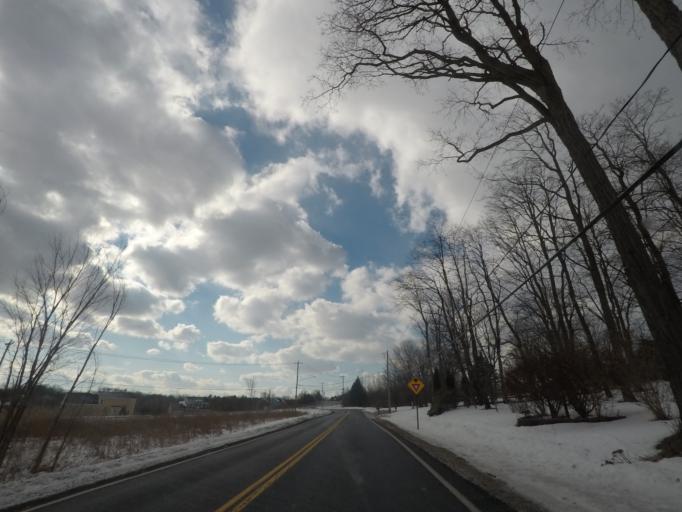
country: US
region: New York
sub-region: Saratoga County
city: Country Knolls
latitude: 42.8953
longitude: -73.7493
